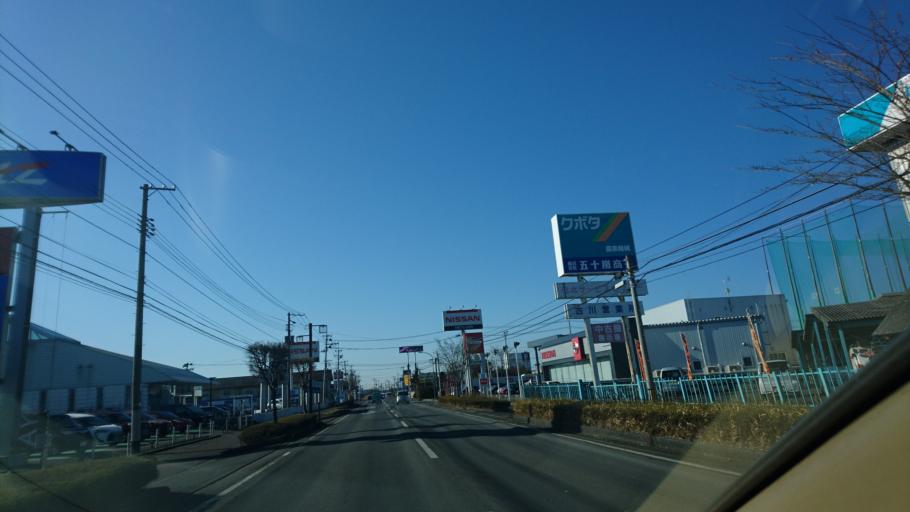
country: JP
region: Miyagi
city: Furukawa
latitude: 38.6008
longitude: 140.9783
